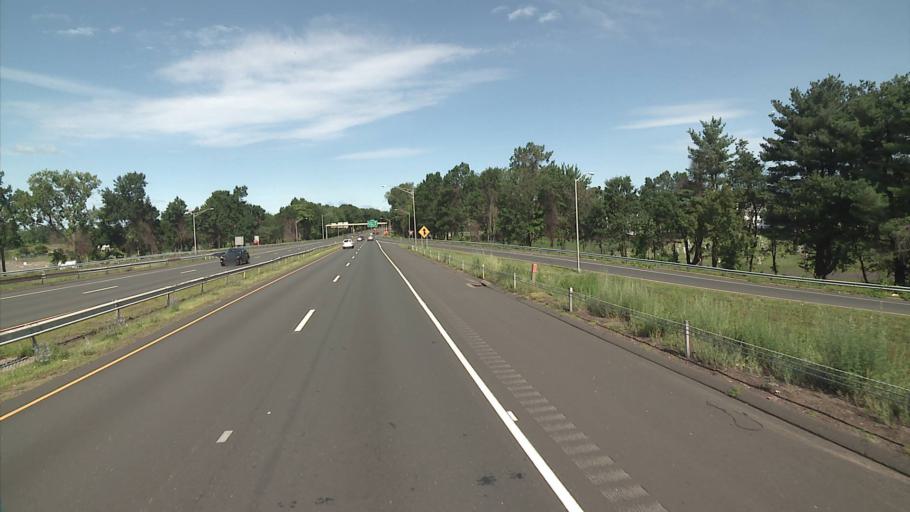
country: US
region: Connecticut
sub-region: Hartford County
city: Wethersfield
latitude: 41.7420
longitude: -72.6346
